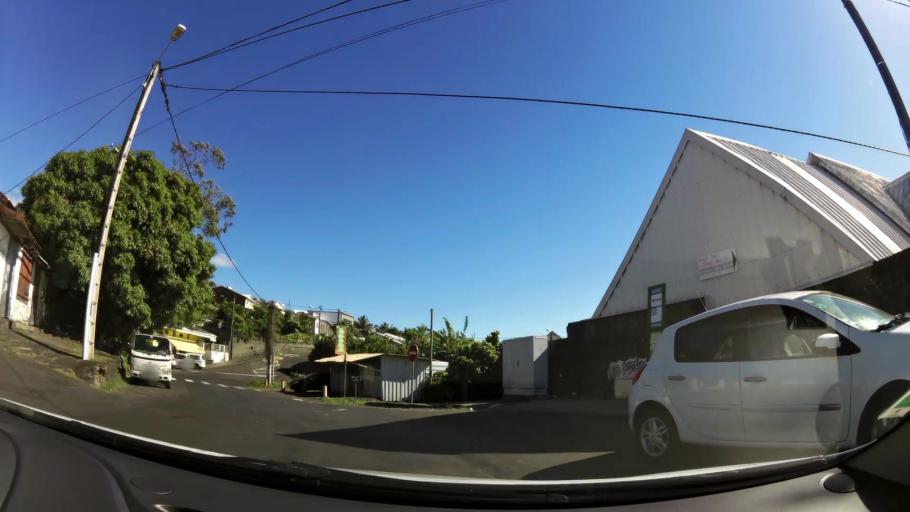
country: RE
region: Reunion
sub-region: Reunion
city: Saint-Denis
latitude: -20.9137
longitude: 55.4839
